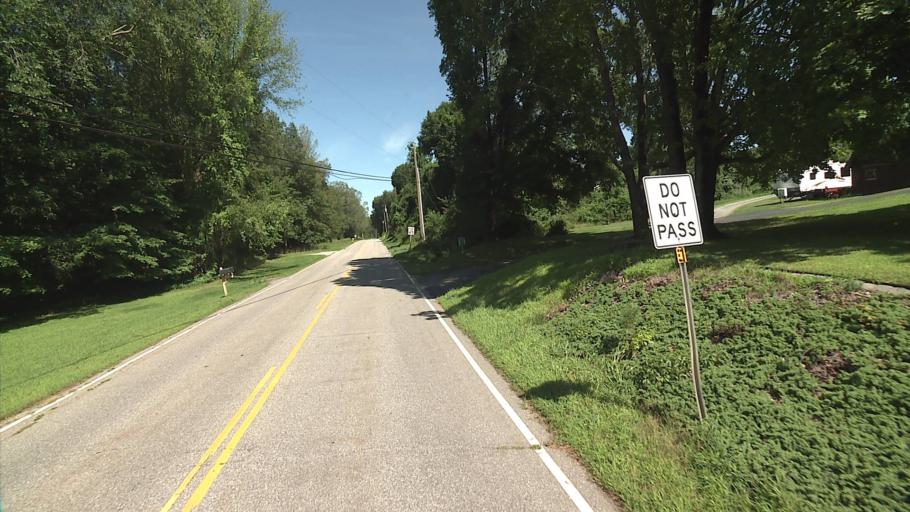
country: US
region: Connecticut
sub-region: New London County
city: Baltic
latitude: 41.6457
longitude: -72.0904
